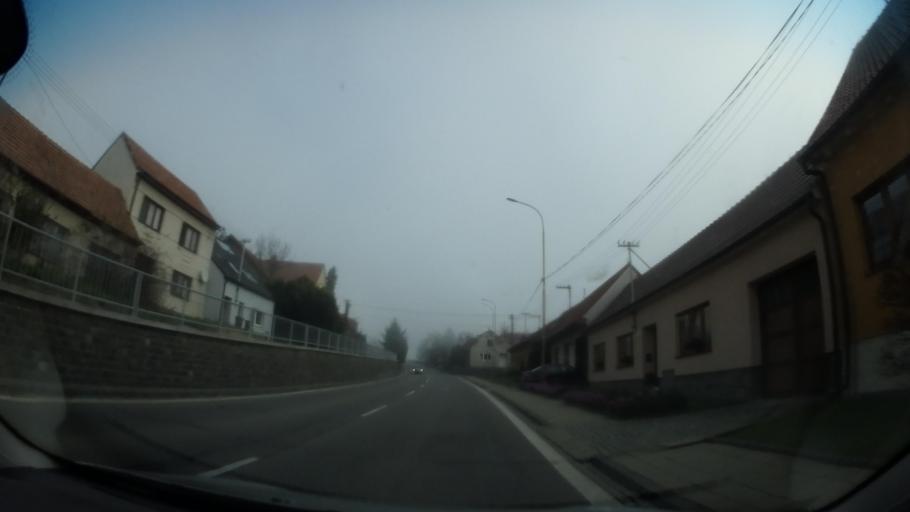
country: CZ
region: South Moravian
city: Damborice
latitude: 49.0411
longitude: 16.9701
